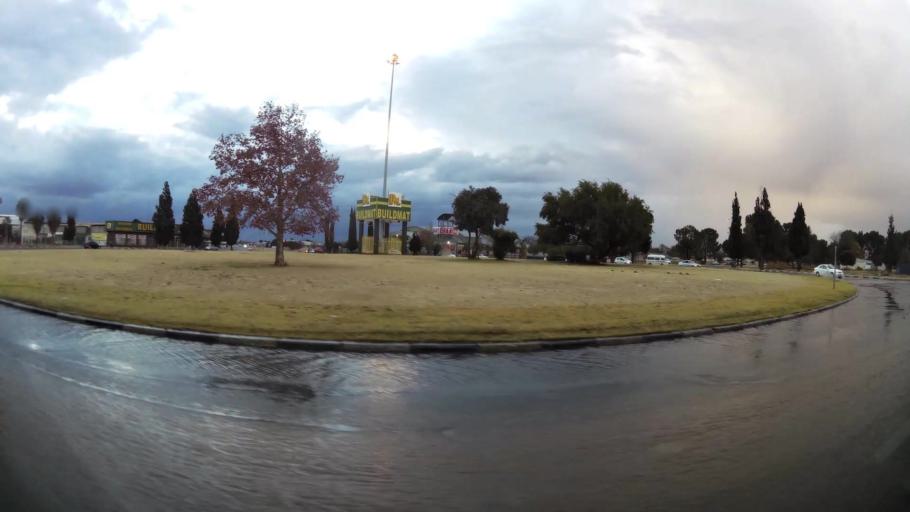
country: ZA
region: Orange Free State
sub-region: Lejweleputswa District Municipality
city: Welkom
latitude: -27.9753
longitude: 26.7631
